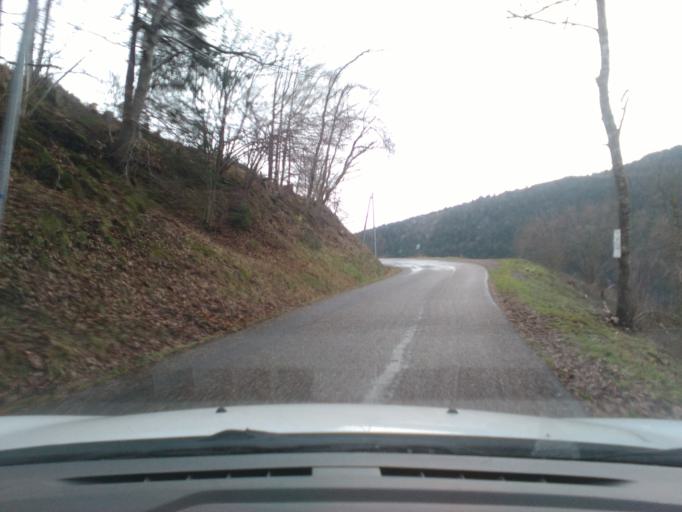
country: FR
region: Lorraine
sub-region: Departement des Vosges
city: La Bresse
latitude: 47.9745
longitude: 6.8626
